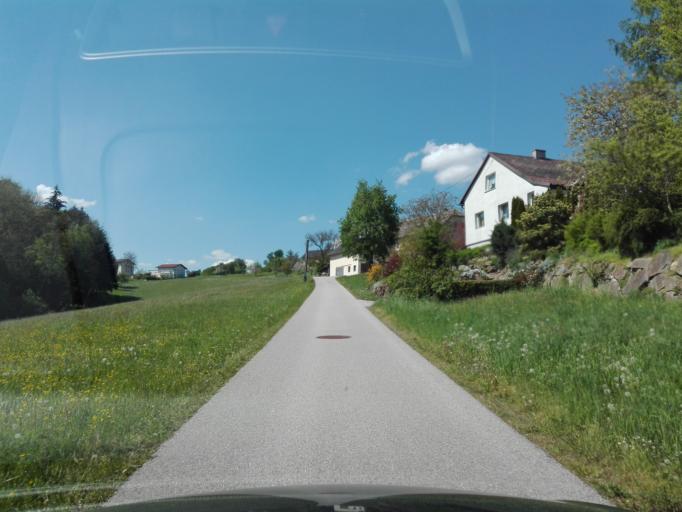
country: AT
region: Upper Austria
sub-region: Politischer Bezirk Urfahr-Umgebung
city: Feldkirchen an der Donau
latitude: 48.3454
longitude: 13.9647
